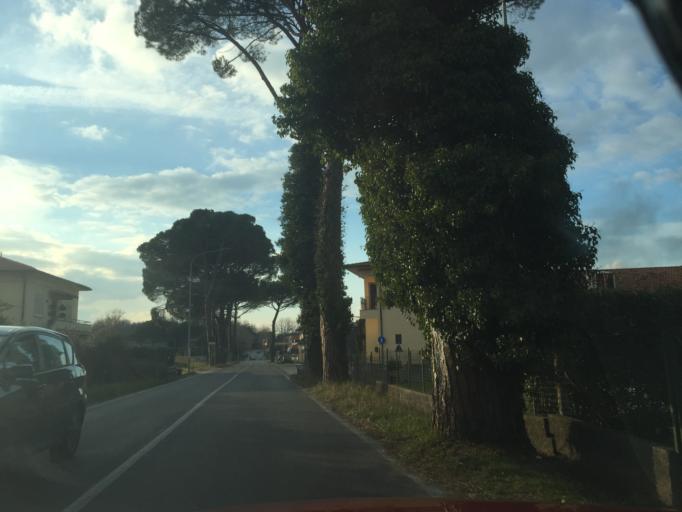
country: IT
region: Tuscany
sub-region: Provincia di Pistoia
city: Lamporecchio
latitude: 43.8176
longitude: 10.8889
